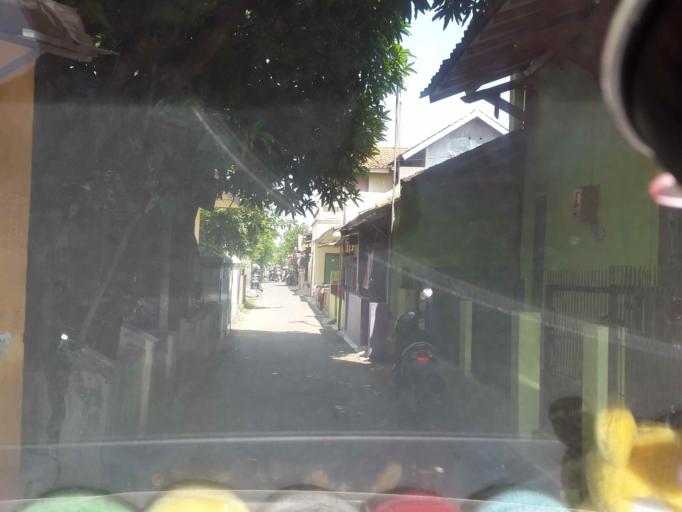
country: ID
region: Central Java
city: Tegal
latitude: -6.8609
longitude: 109.1461
